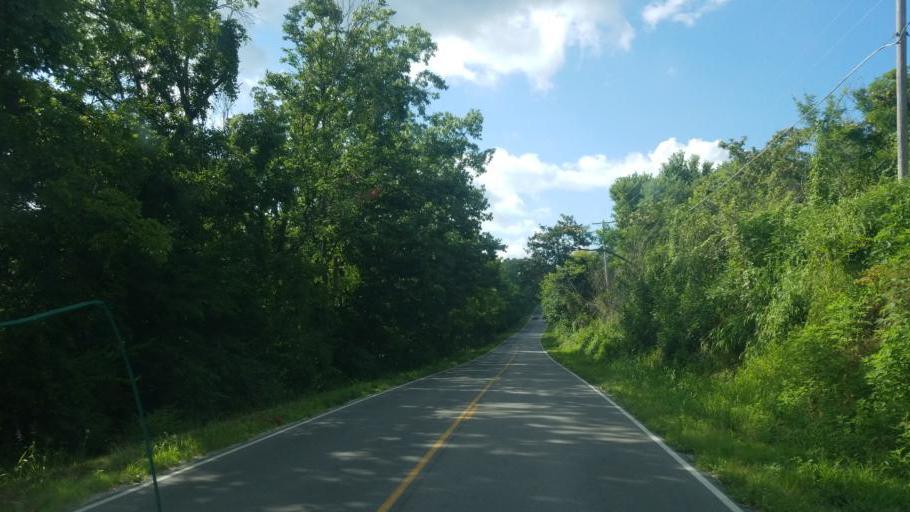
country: US
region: Illinois
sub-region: Union County
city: Cobden
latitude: 37.5648
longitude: -89.3101
